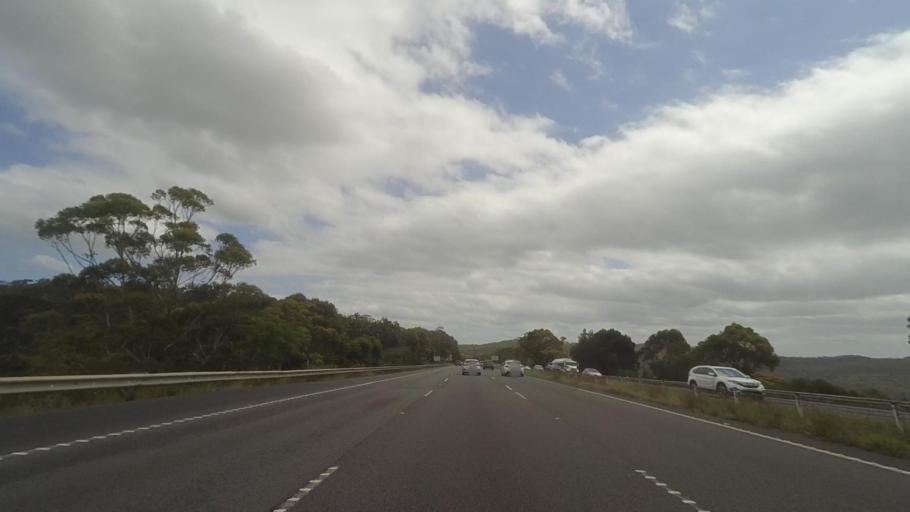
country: AU
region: New South Wales
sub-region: Gosford Shire
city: Point Clare
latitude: -33.4341
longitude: 151.2221
